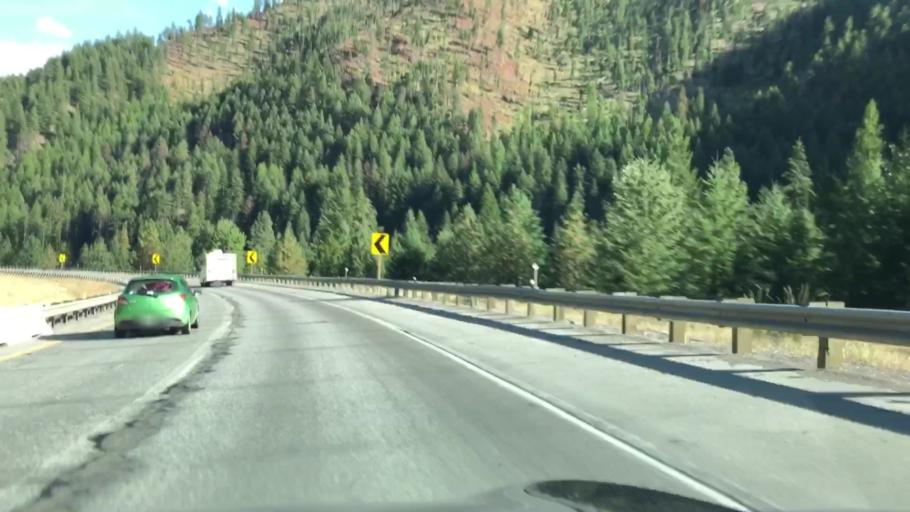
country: US
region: Montana
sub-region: Mineral County
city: Superior
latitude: 47.3020
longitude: -115.2002
